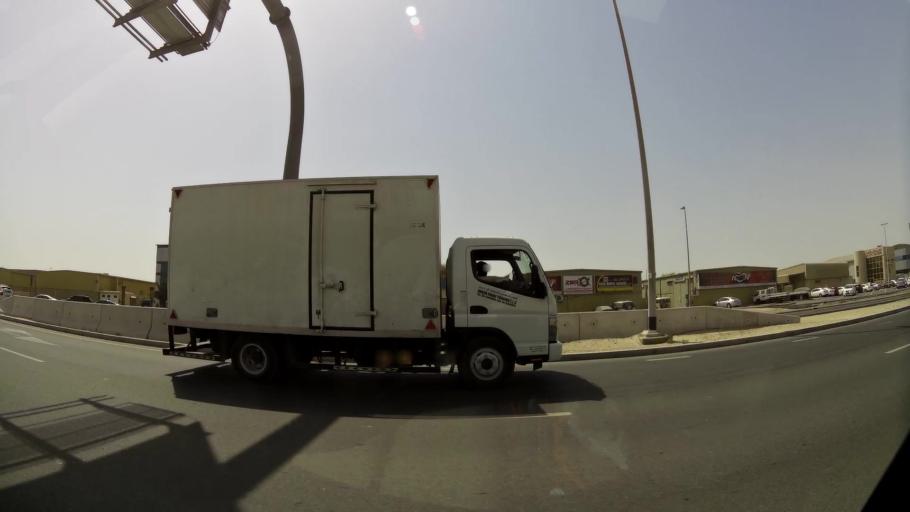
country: AE
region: Dubai
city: Dubai
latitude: 25.1597
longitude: 55.2391
